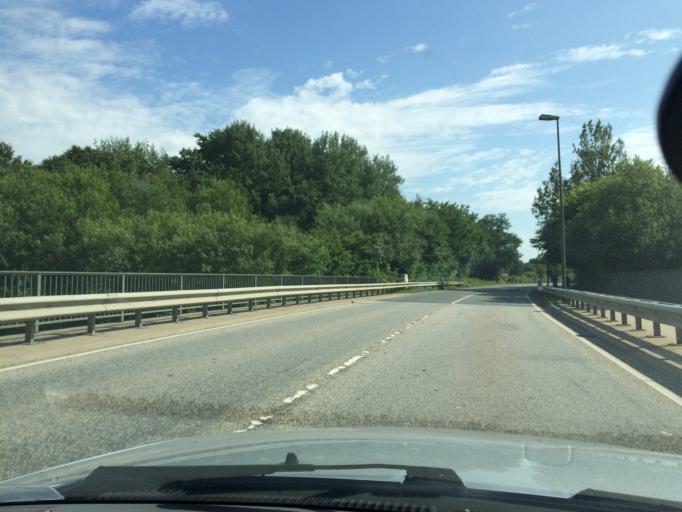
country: DE
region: Schleswig-Holstein
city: Jarplund-Weding
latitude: 54.7573
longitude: 9.4362
